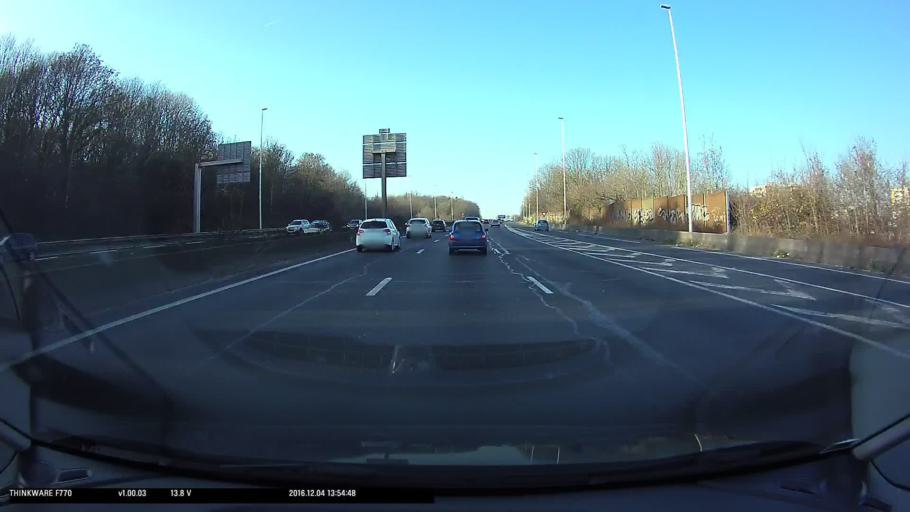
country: FR
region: Ile-de-France
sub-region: Departement du Val-d'Oise
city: Franconville
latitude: 48.9769
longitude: 2.2349
